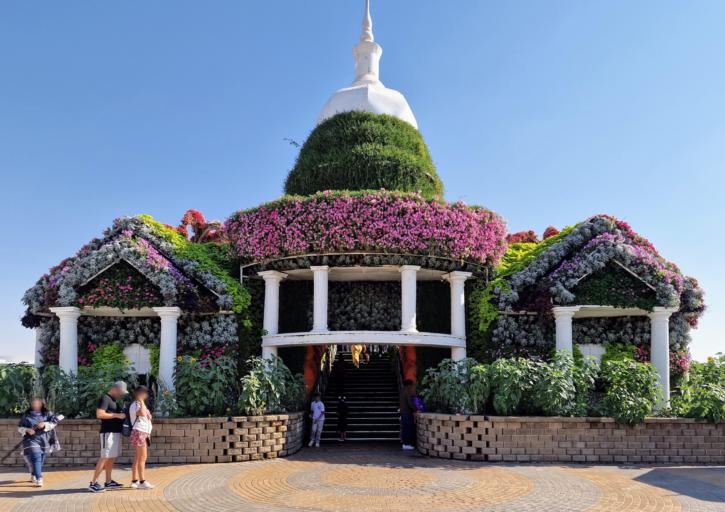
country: AE
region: Dubai
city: Dubai
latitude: 25.0600
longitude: 55.2445
